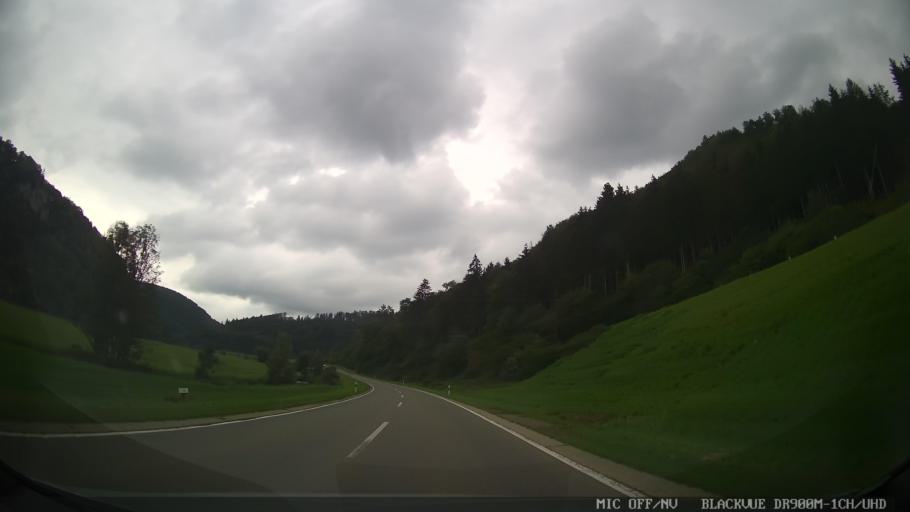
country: DE
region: Baden-Wuerttemberg
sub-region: Freiburg Region
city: Barenthal
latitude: 48.0672
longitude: 8.9258
